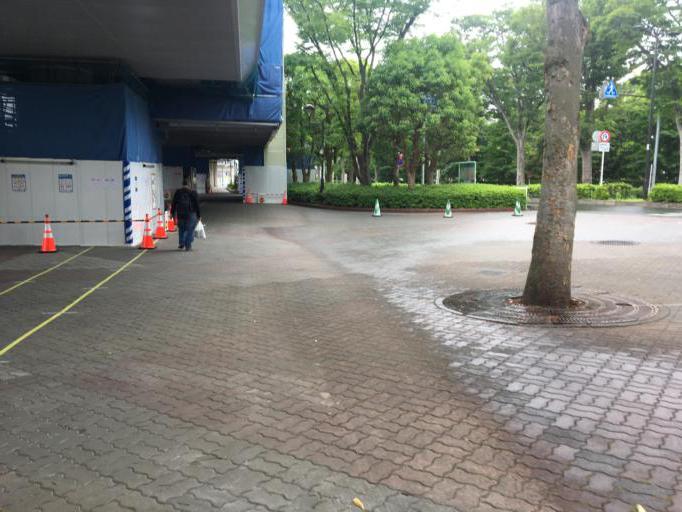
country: JP
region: Tokyo
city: Kokubunji
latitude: 35.6645
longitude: 139.4806
